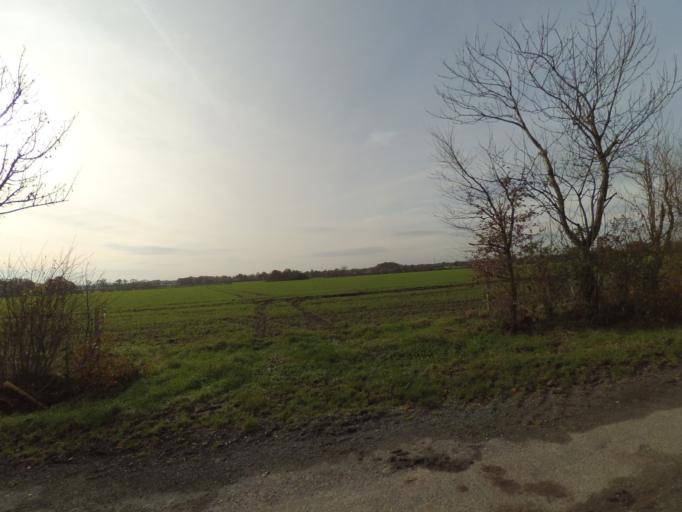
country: FR
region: Pays de la Loire
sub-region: Departement de la Loire-Atlantique
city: La Planche
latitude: 47.0062
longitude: -1.3994
